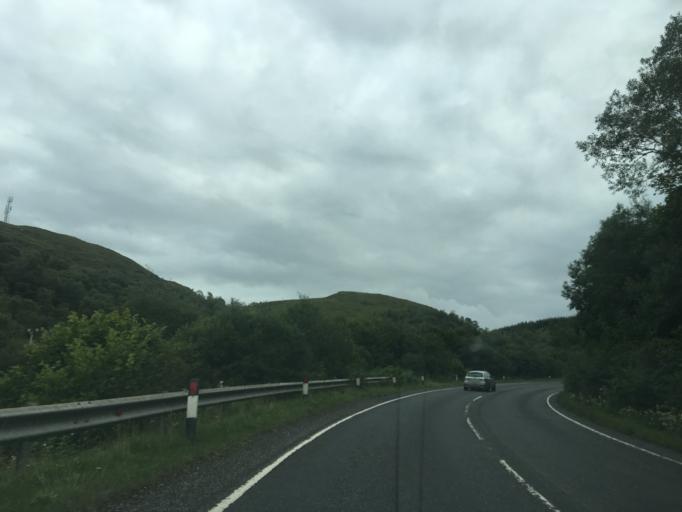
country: GB
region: Scotland
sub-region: Argyll and Bute
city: Oban
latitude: 56.3079
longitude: -5.4670
